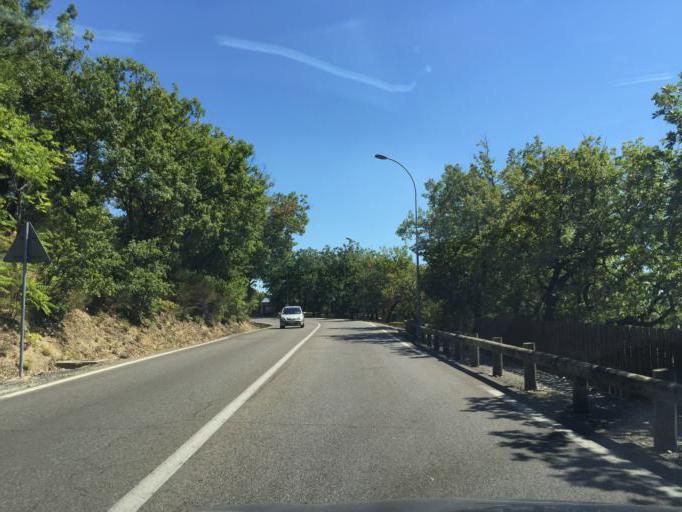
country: FR
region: Provence-Alpes-Cote d'Azur
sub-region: Departement des Alpes-de-Haute-Provence
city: Volonne
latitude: 44.0787
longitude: 5.9962
